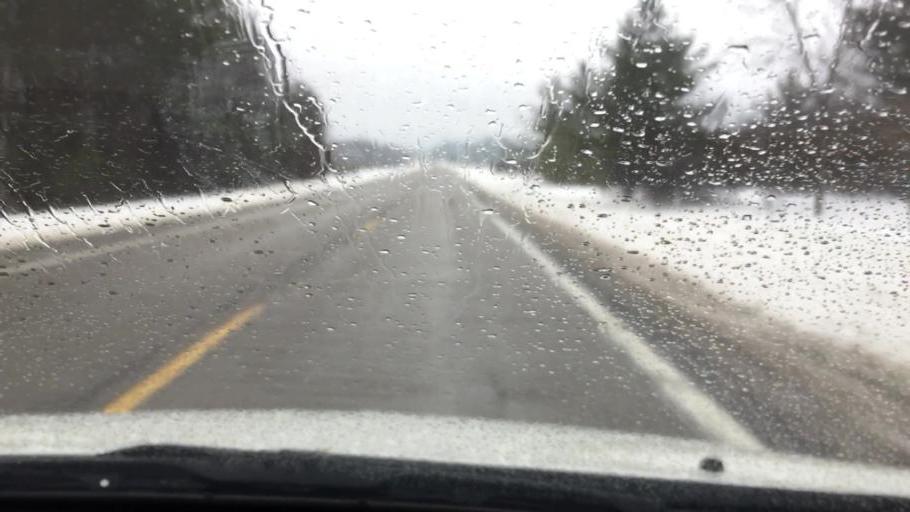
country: US
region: Michigan
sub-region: Charlevoix County
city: East Jordan
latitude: 45.1040
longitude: -85.1210
